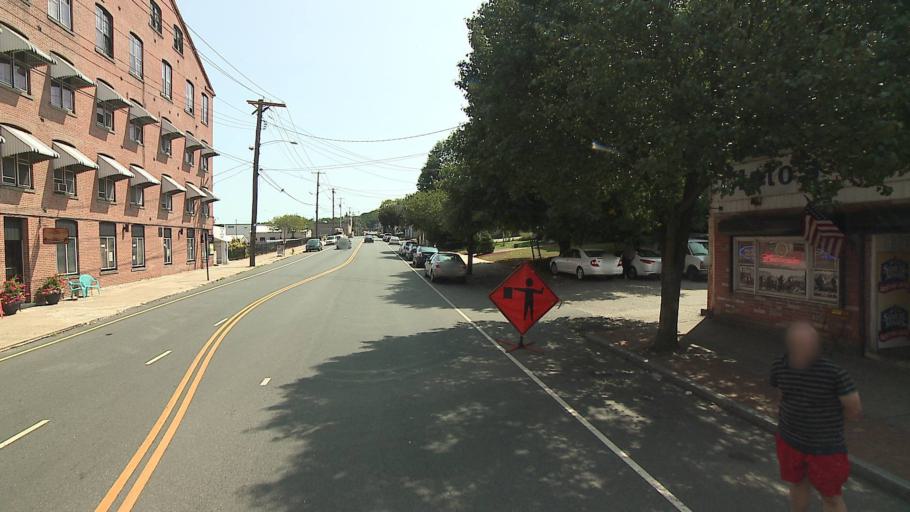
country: US
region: Connecticut
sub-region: Fairfield County
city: Shelton
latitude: 41.3165
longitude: -73.0927
